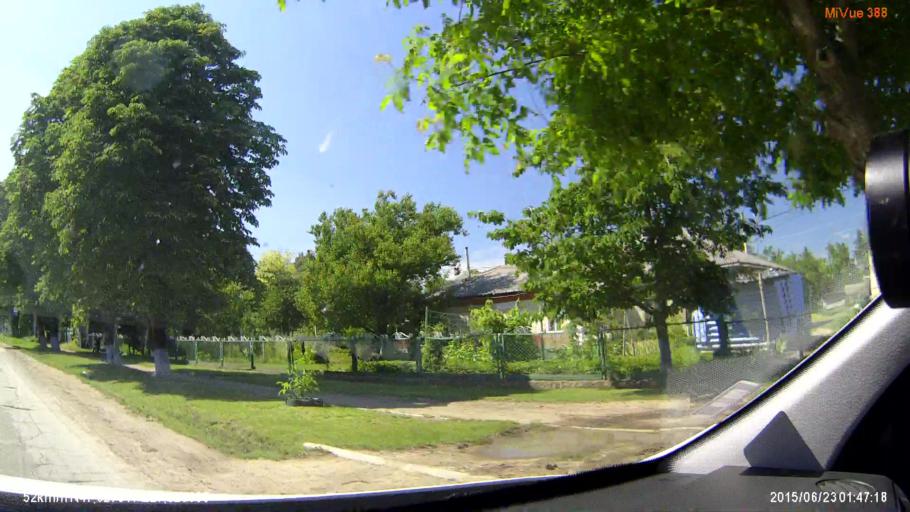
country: RO
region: Iasi
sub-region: Comuna Victoria
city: Victoria
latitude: 47.3270
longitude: 27.6255
